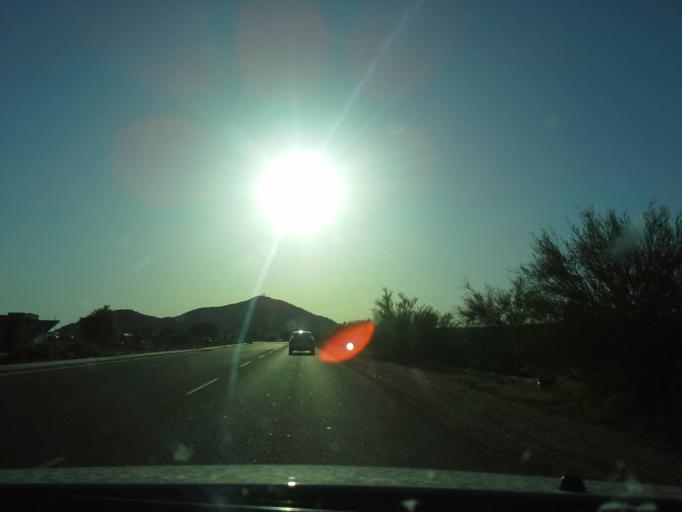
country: US
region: Arizona
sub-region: Maricopa County
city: Paradise Valley
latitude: 33.6762
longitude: -112.0159
